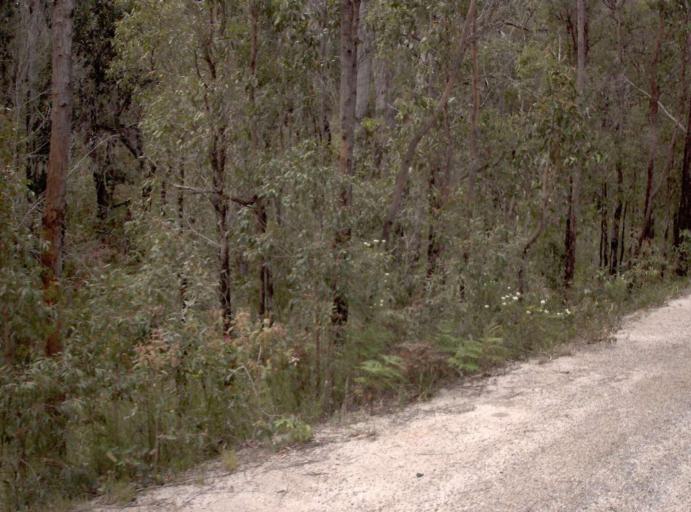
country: AU
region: New South Wales
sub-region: Bega Valley
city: Eden
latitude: -37.4024
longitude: 149.6680
